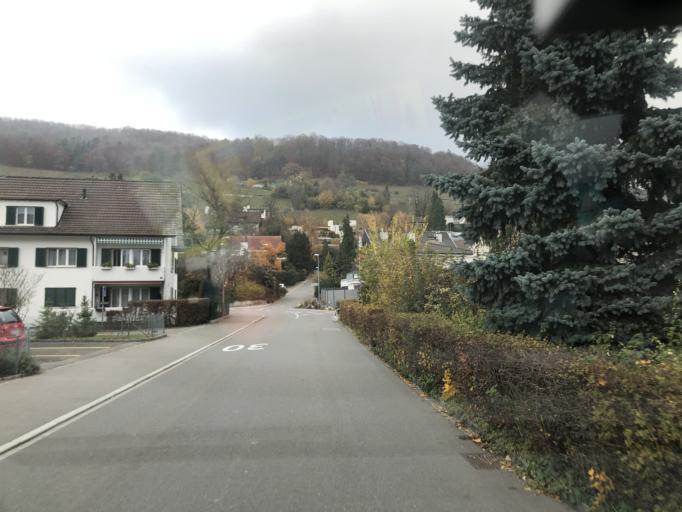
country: CH
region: Aargau
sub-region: Bezirk Baden
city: Wettingen
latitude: 47.4687
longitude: 8.3300
